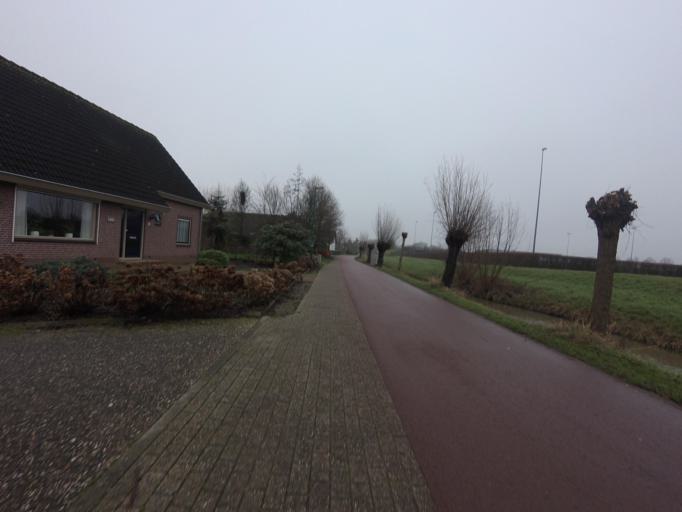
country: NL
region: Utrecht
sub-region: Gemeente Houten
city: Houten
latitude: 52.0205
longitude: 5.1605
